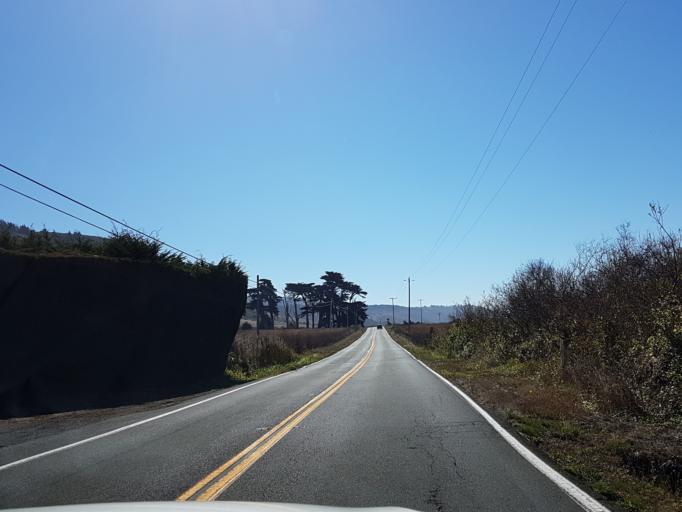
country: US
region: California
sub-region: Mendocino County
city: Boonville
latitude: 39.0799
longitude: -123.6961
